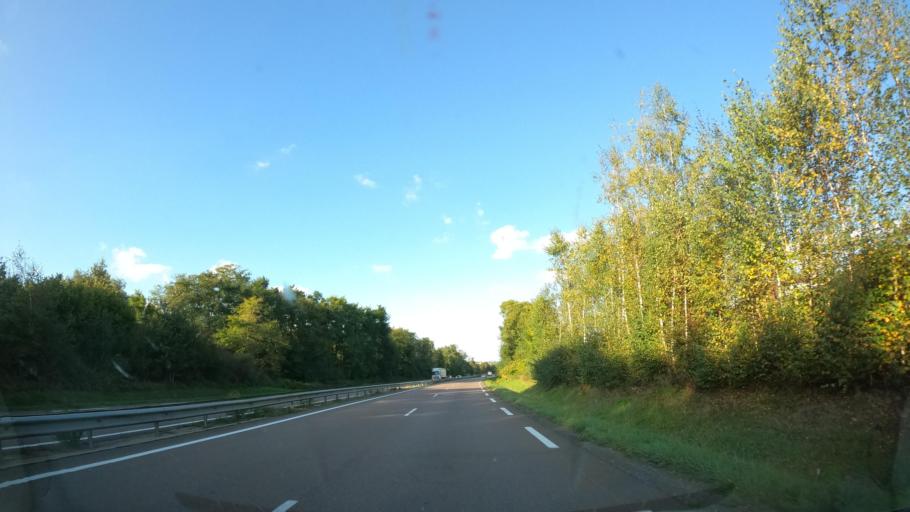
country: FR
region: Bourgogne
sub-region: Departement de Saone-et-Loire
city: Montceau-les-Mines
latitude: 46.6586
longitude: 4.3314
